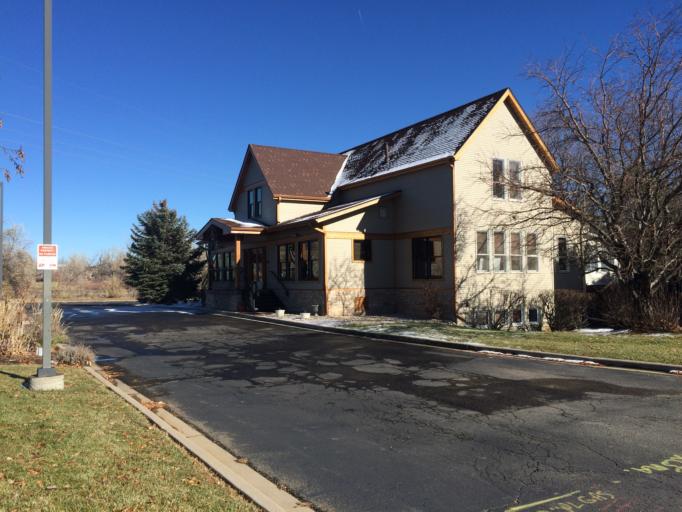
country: US
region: Colorado
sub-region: Boulder County
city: Louisville
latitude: 39.9903
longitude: -105.1241
